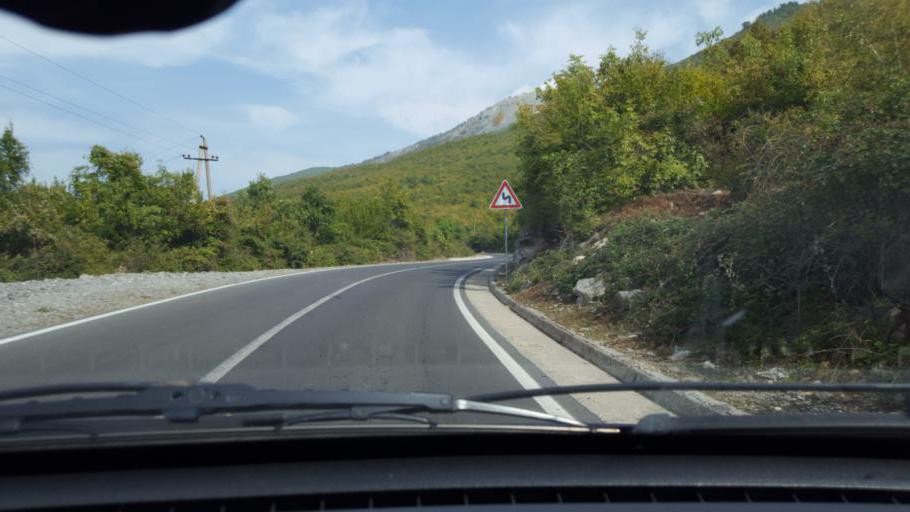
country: AL
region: Shkoder
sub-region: Rrethi i Malesia e Madhe
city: Kastrat
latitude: 42.3818
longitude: 19.4929
